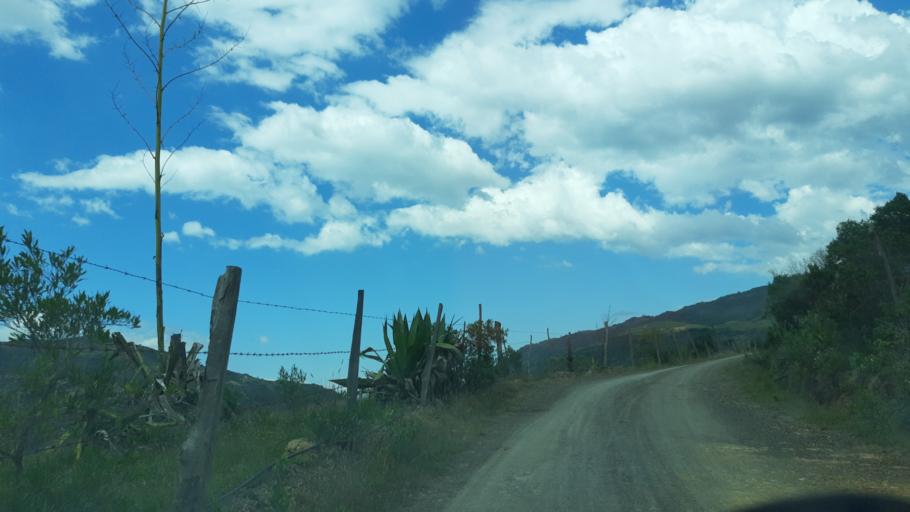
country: CO
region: Boyaca
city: Santa Sofia
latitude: 5.7033
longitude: -73.5649
